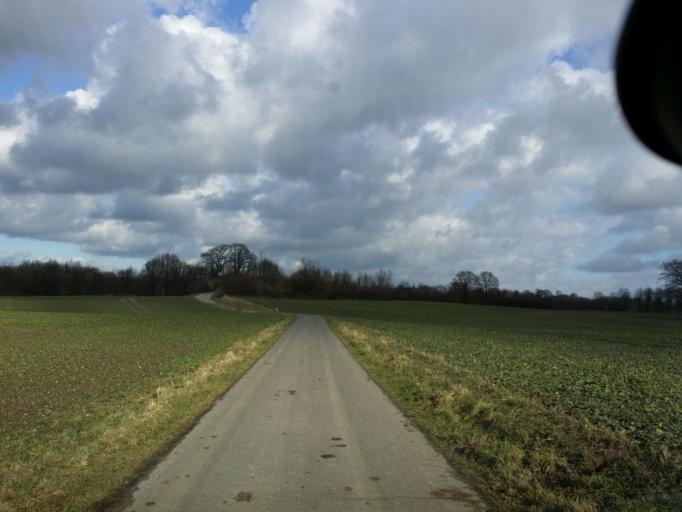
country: DE
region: Schleswig-Holstein
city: Bredenbek
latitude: 54.3111
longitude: 9.8902
